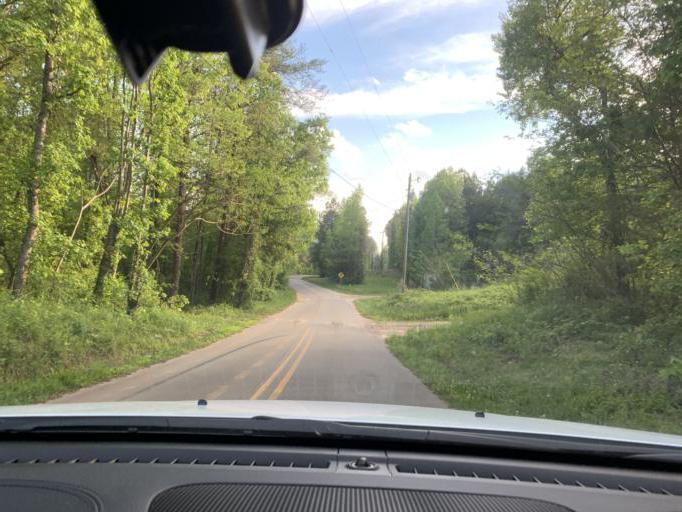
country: US
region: Georgia
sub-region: Dawson County
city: Dawsonville
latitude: 34.3331
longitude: -84.1702
